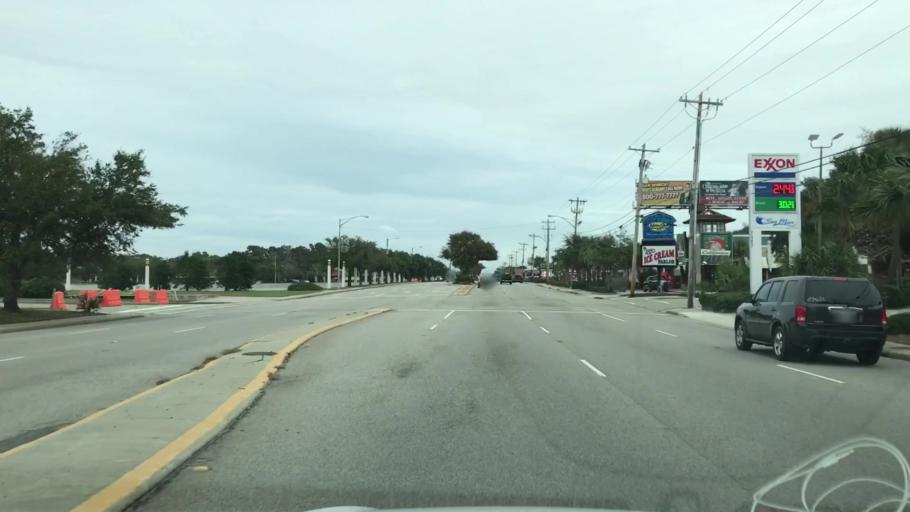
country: US
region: South Carolina
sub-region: Horry County
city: Myrtle Beach
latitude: 33.7055
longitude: -78.8683
